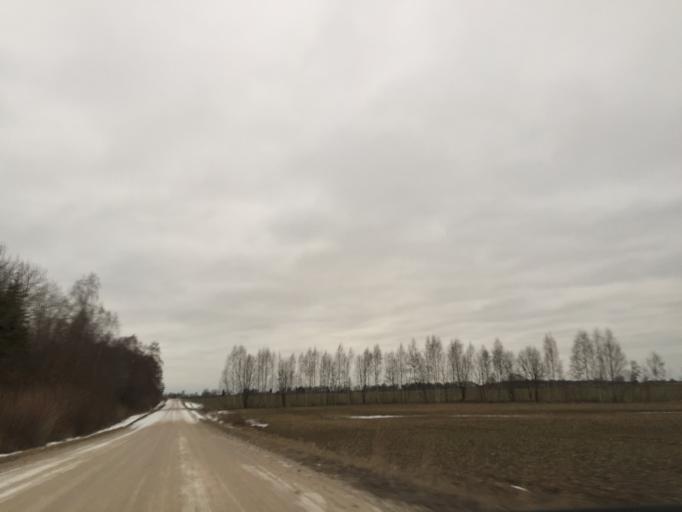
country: LT
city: Zagare
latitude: 56.3020
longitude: 23.2605
